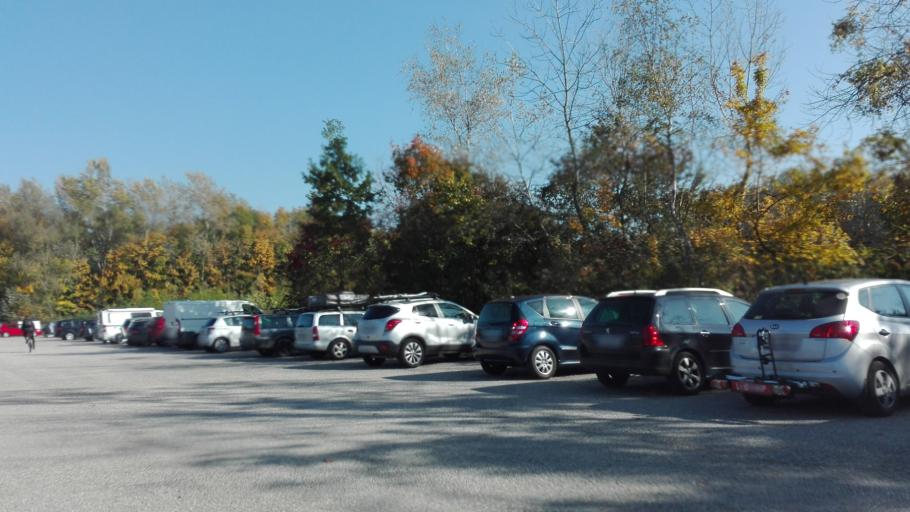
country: AT
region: Upper Austria
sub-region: Politischer Bezirk Urfahr-Umgebung
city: Ottensheim
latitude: 48.3150
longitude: 14.1533
